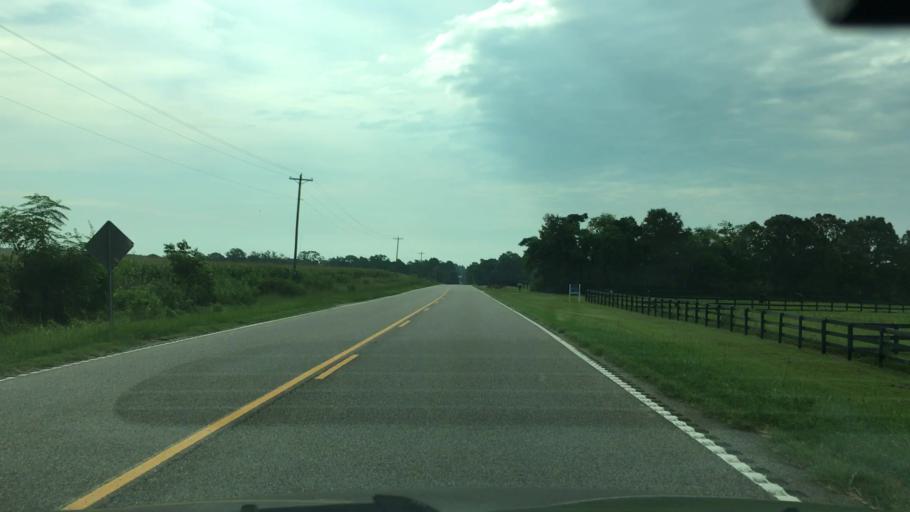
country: US
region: South Carolina
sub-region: Lexington County
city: Batesburg-Leesville
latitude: 33.6899
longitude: -81.4697
